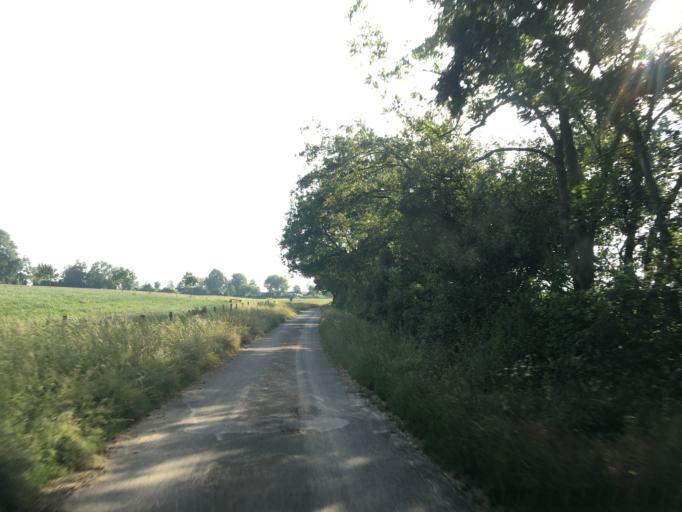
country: DE
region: North Rhine-Westphalia
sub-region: Regierungsbezirk Munster
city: Altenberge
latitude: 52.0181
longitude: 7.5322
